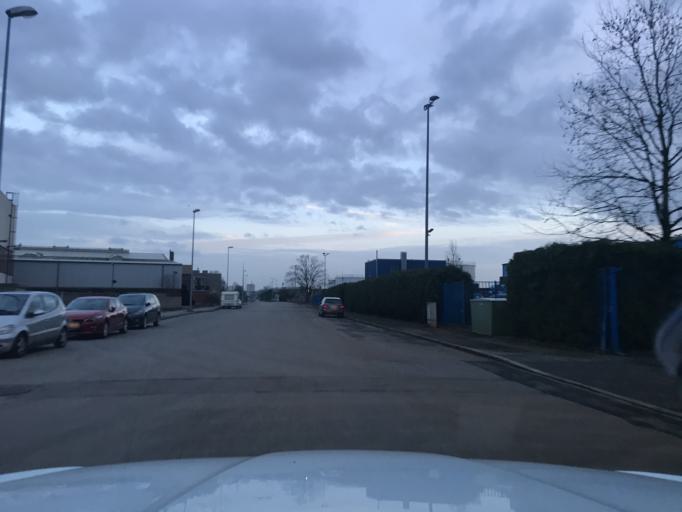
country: DE
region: North Rhine-Westphalia
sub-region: Regierungsbezirk Dusseldorf
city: Muelheim (Ruhr)
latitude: 51.4382
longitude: 6.8418
